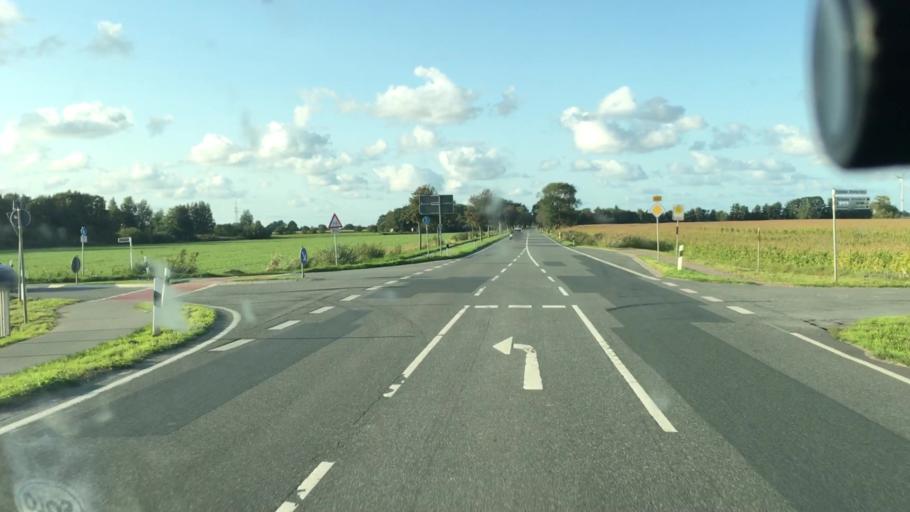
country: DE
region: Lower Saxony
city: Werdum
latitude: 53.6515
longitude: 7.7899
